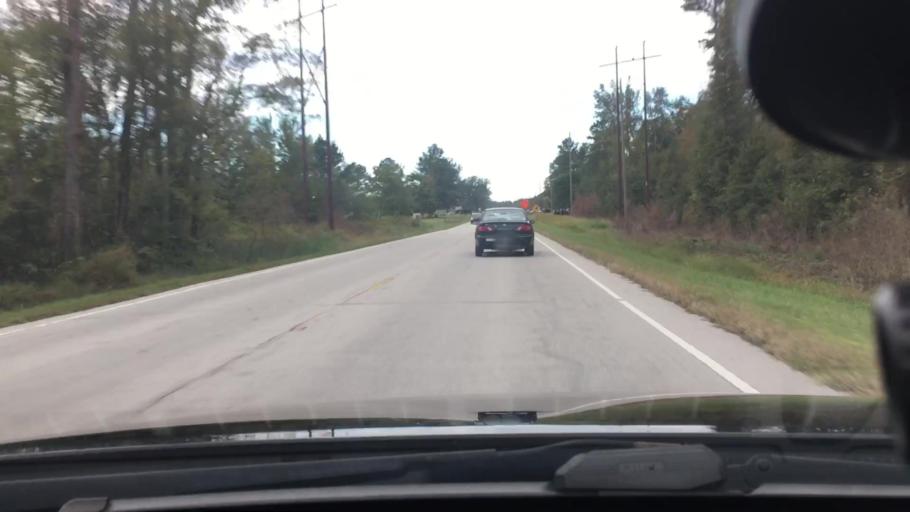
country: US
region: North Carolina
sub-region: Pitt County
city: Windsor
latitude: 35.4913
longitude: -77.3067
